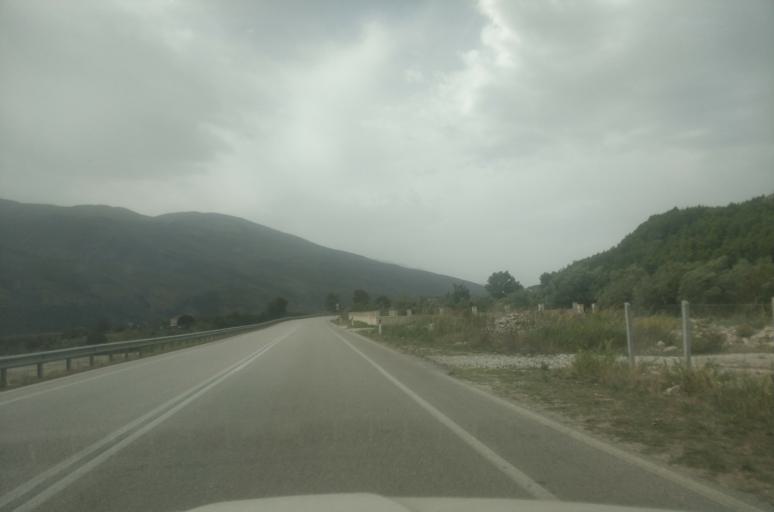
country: AL
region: Gjirokaster
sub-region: Rrethi i Tepelenes
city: Memaliaj
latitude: 40.3521
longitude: 19.9586
